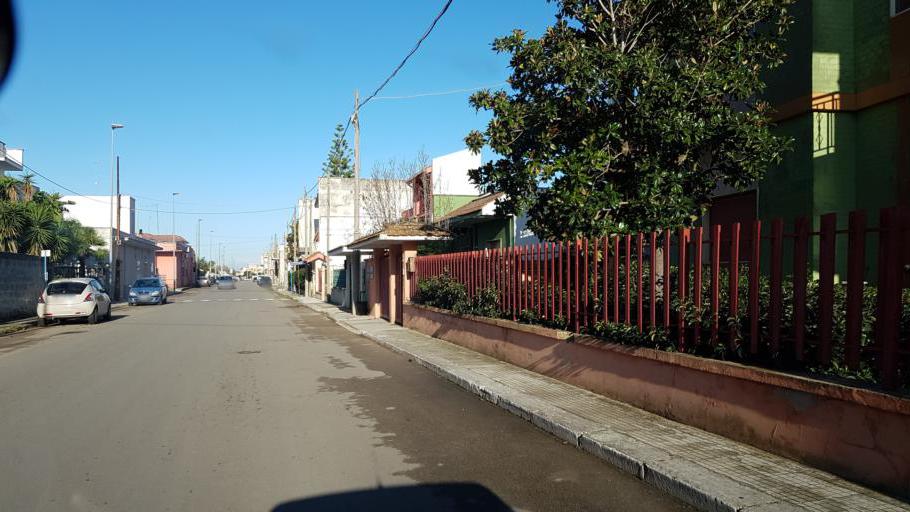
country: IT
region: Apulia
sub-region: Provincia di Brindisi
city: Torchiarolo
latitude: 40.4818
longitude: 18.0508
